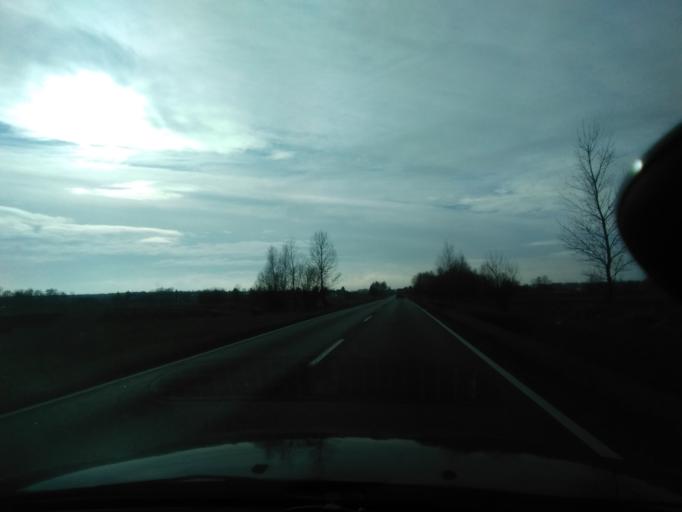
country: PL
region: Subcarpathian Voivodeship
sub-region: Powiat krosnienski
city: Kroscienko Wyzne
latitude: 49.6661
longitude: 21.8433
